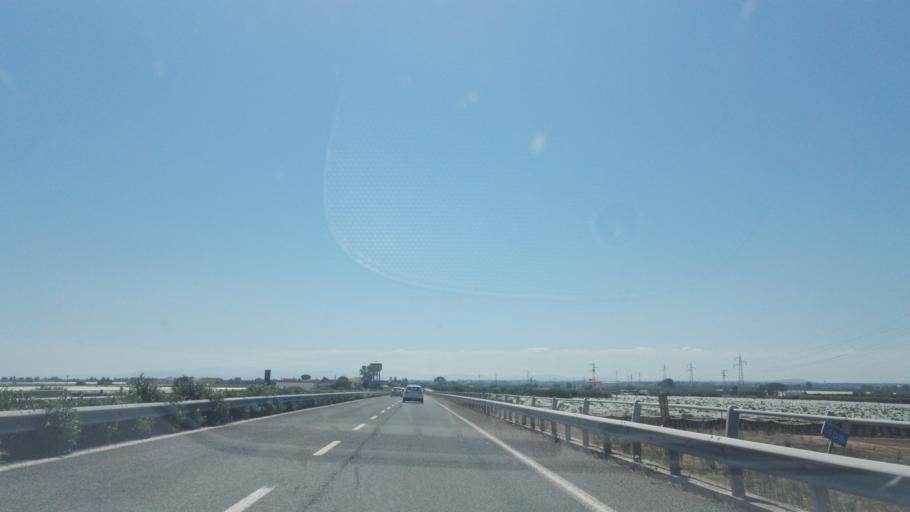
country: IT
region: Apulia
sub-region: Provincia di Taranto
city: Marina di Ginosa
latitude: 40.4415
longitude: 16.8469
